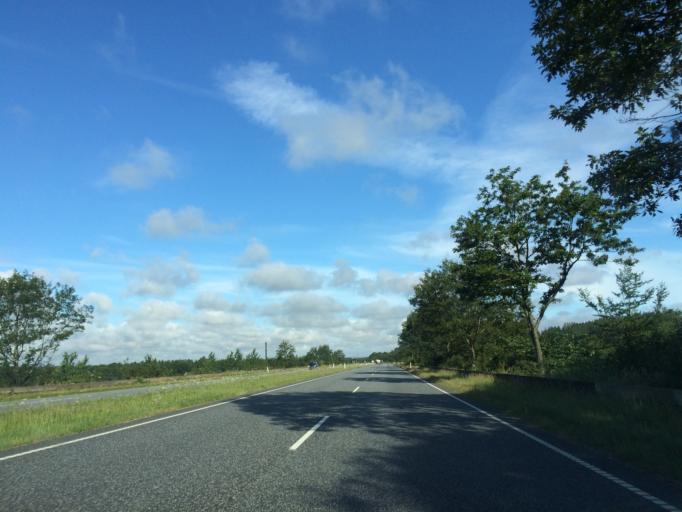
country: DK
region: Central Jutland
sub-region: Viborg Kommune
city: Viborg
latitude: 56.4143
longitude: 9.4184
